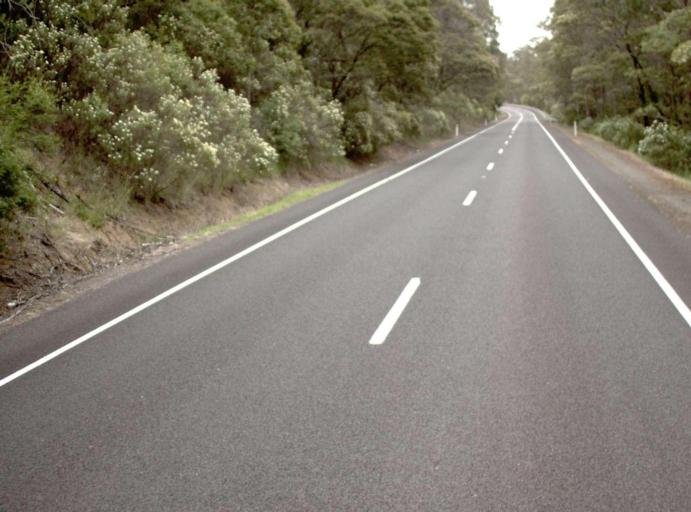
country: AU
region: New South Wales
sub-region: Bombala
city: Bombala
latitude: -37.2531
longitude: 149.2463
